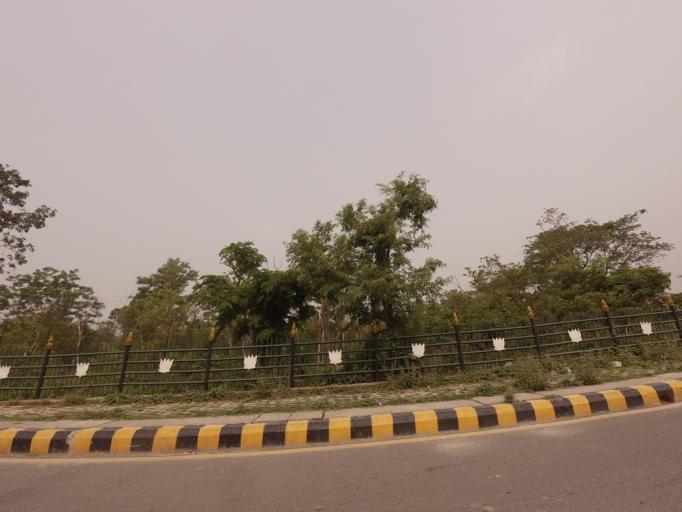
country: IN
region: Uttar Pradesh
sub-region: Maharajganj
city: Nautanwa
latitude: 27.4736
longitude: 83.2838
